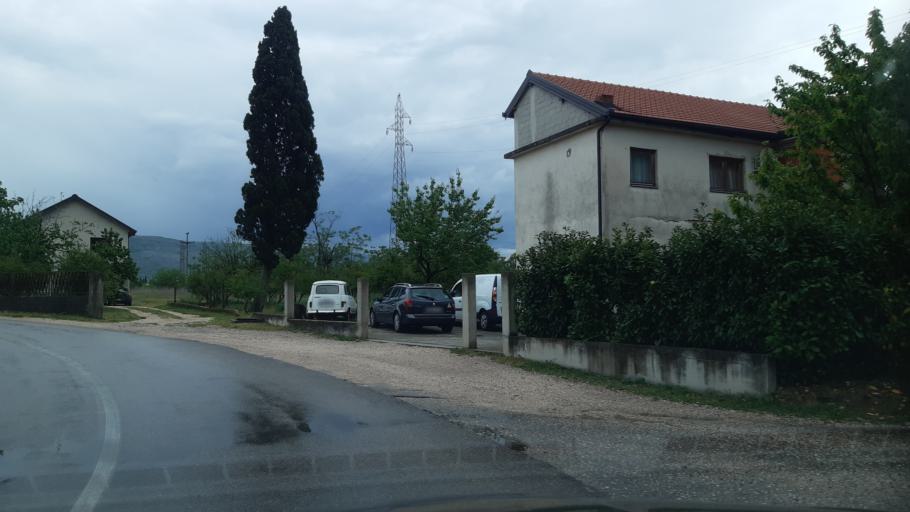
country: BA
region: Federation of Bosnia and Herzegovina
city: Rodoc
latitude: 43.3047
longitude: 17.7978
